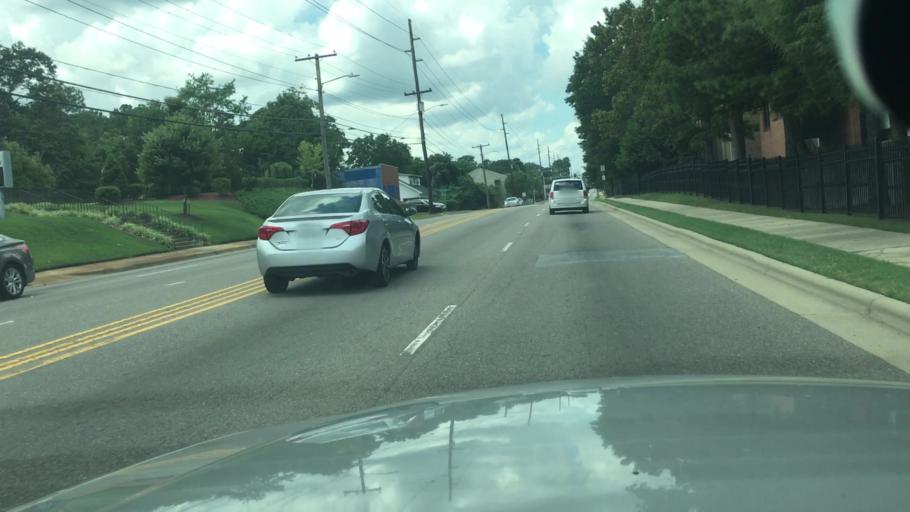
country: US
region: North Carolina
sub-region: Cumberland County
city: Fayetteville
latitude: 35.0724
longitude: -78.8951
